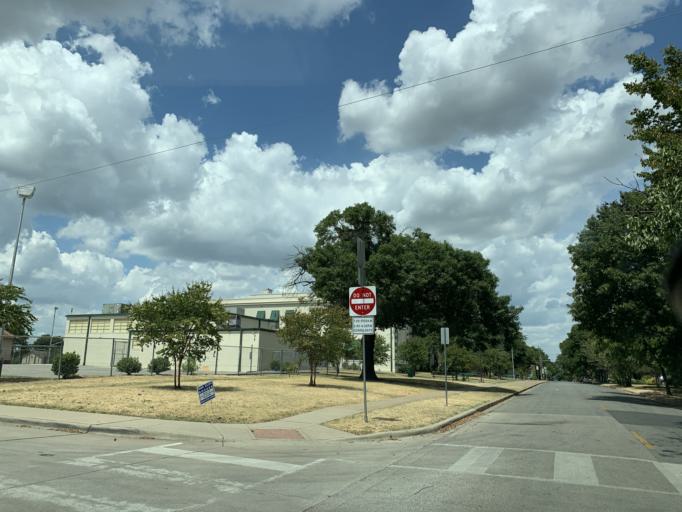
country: US
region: Texas
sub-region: Dallas County
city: Cockrell Hill
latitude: 32.7509
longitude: -96.8465
